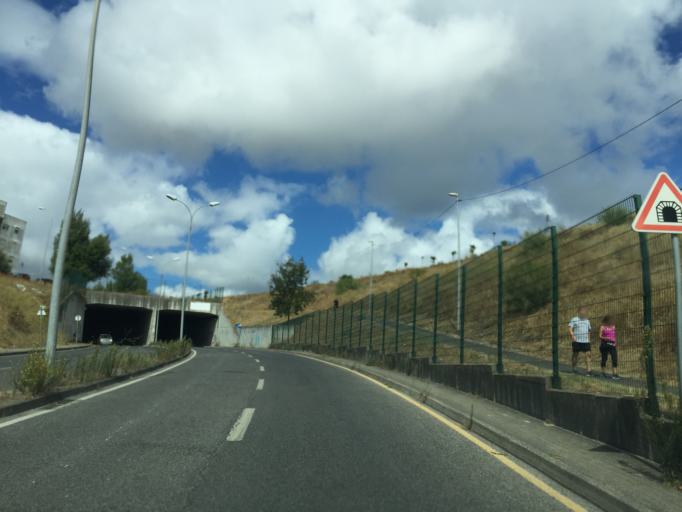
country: PT
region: Lisbon
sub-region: Amadora
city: Amadora
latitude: 38.7723
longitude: -9.2261
